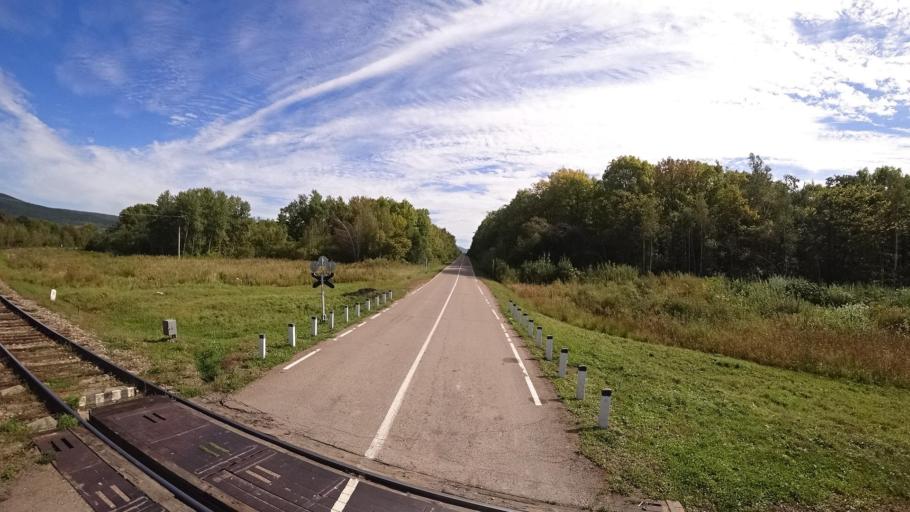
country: RU
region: Primorskiy
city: Yakovlevka
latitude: 44.4060
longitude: 133.5922
